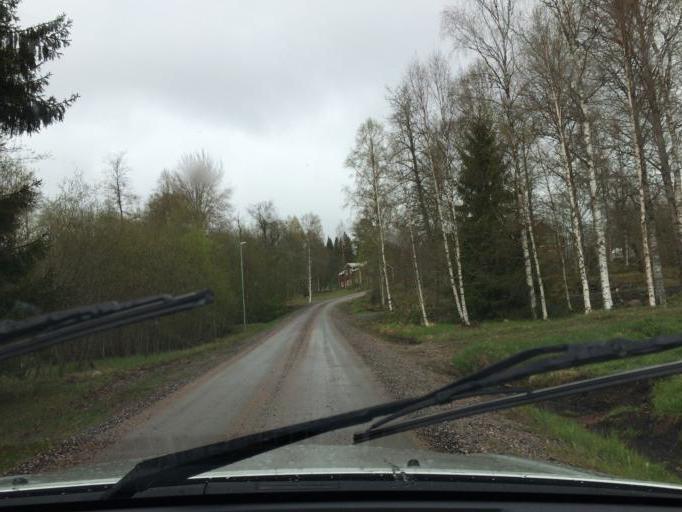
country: SE
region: Dalarna
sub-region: Ludvika Kommun
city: Abborrberget
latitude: 60.0212
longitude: 14.6222
